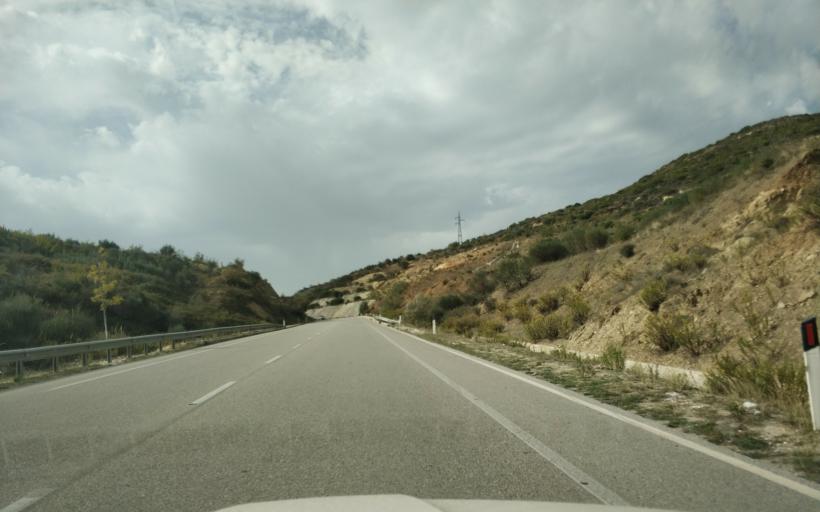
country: AL
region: Gjirokaster
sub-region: Rrethi i Tepelenes
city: Krahes
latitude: 40.3970
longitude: 19.8699
